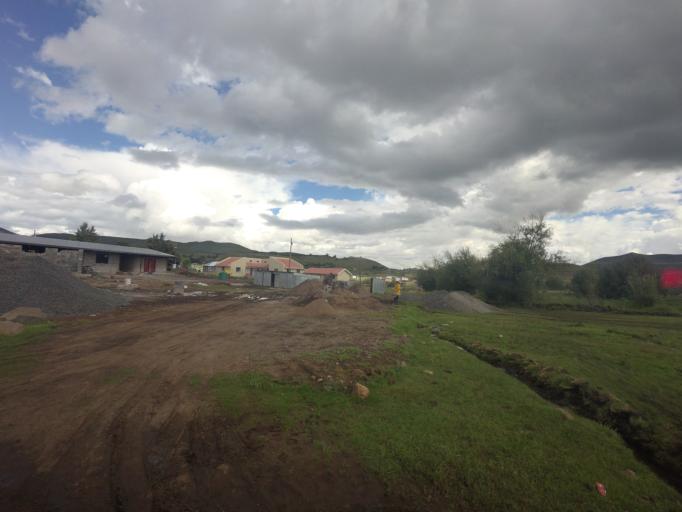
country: LS
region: Maseru
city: Nako
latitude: -29.8404
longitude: 28.0586
